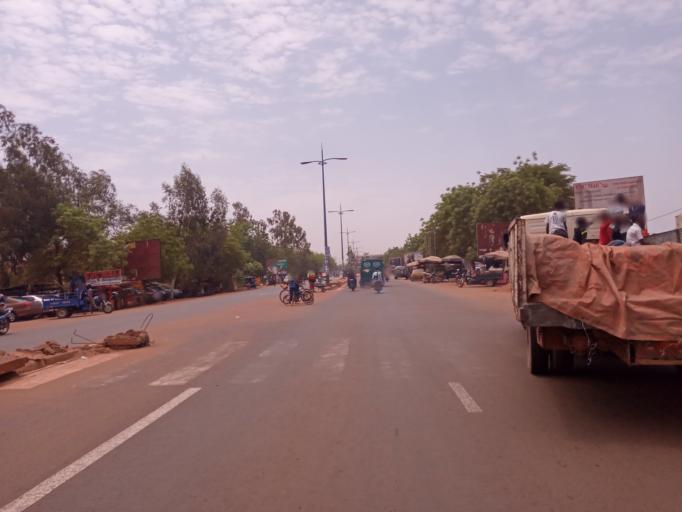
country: ML
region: Bamako
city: Bamako
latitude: 12.5699
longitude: -7.9832
